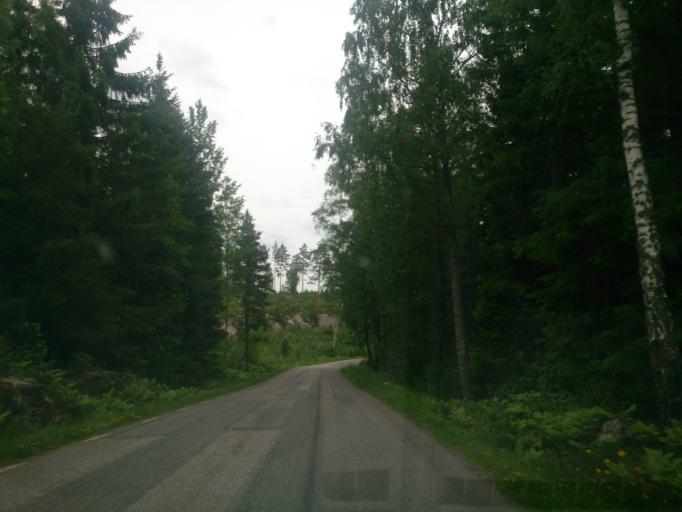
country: SE
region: OEstergoetland
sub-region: Soderkopings Kommun
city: Soederkoeping
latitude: 58.2881
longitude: 16.2408
